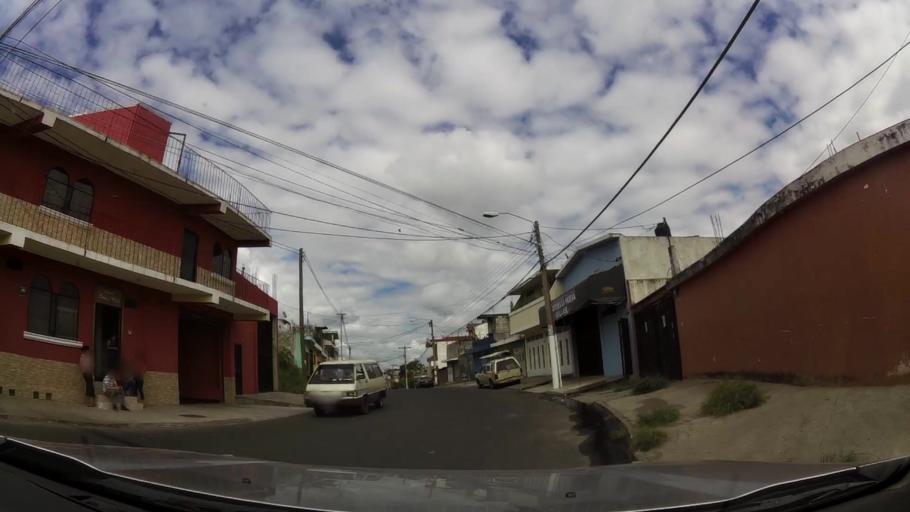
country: GT
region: Guatemala
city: Guatemala City
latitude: 14.6770
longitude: -90.5467
